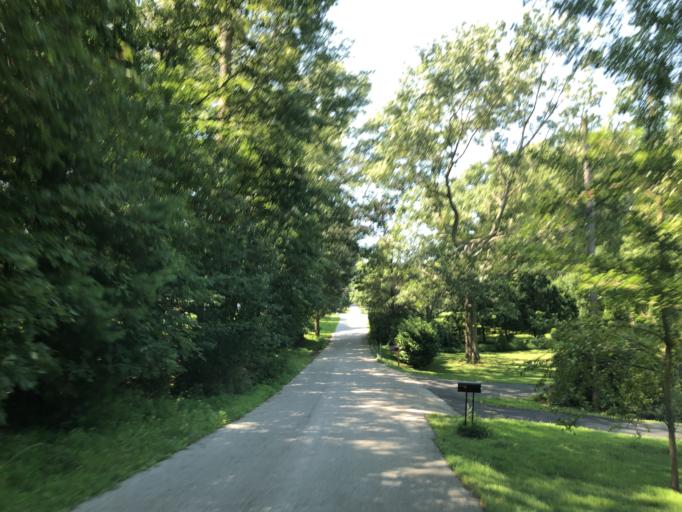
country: US
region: Maryland
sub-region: Carroll County
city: Eldersburg
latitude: 39.4456
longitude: -76.9537
